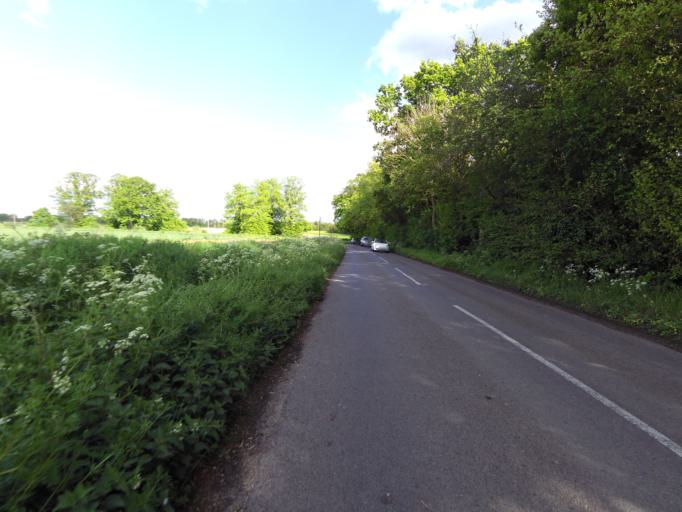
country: GB
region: England
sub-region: Suffolk
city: Stowmarket
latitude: 52.1954
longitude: 0.9651
